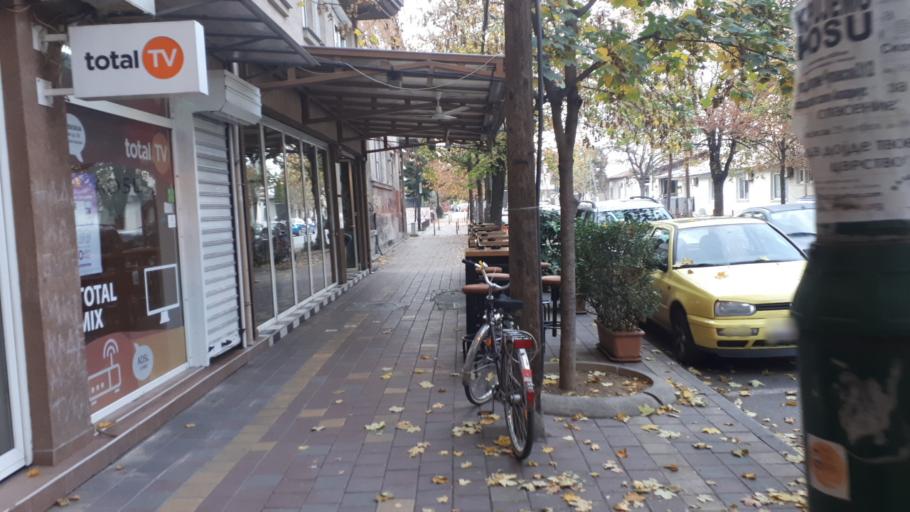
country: MK
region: Karpos
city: Skopje
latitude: 42.0034
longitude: 21.4169
